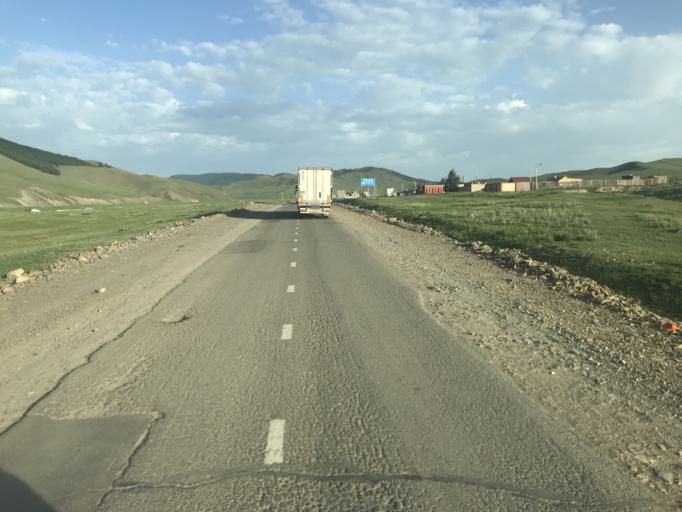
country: MN
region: Central Aimak
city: Bornuur
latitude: 48.4678
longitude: 106.1960
